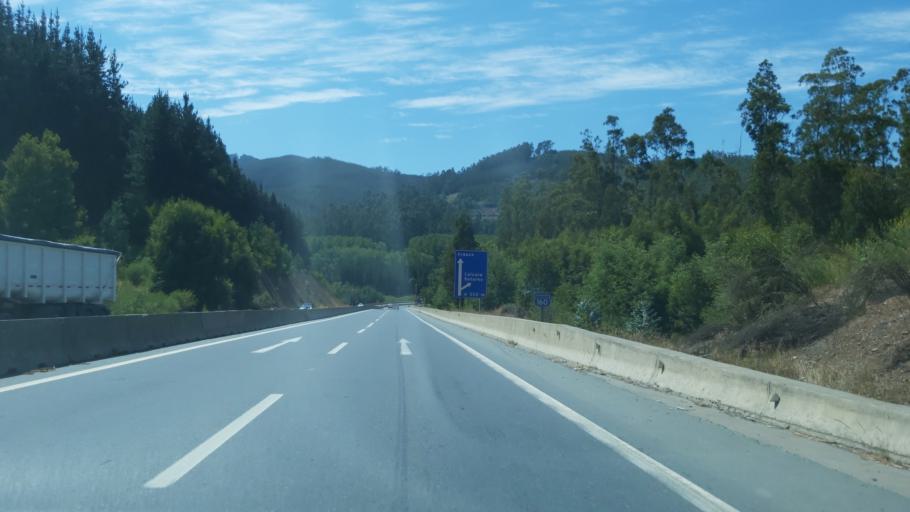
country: CL
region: Biobio
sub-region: Provincia de Concepcion
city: Lota
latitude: -37.1019
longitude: -73.1416
